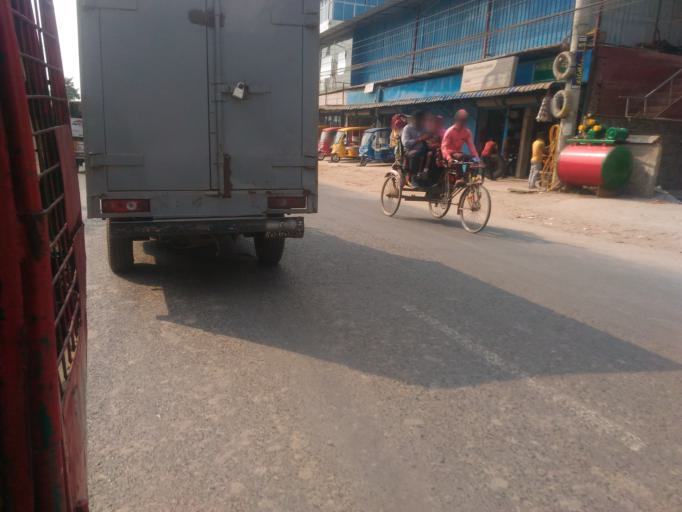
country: BD
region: Dhaka
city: Tungi
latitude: 23.9915
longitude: 90.3943
